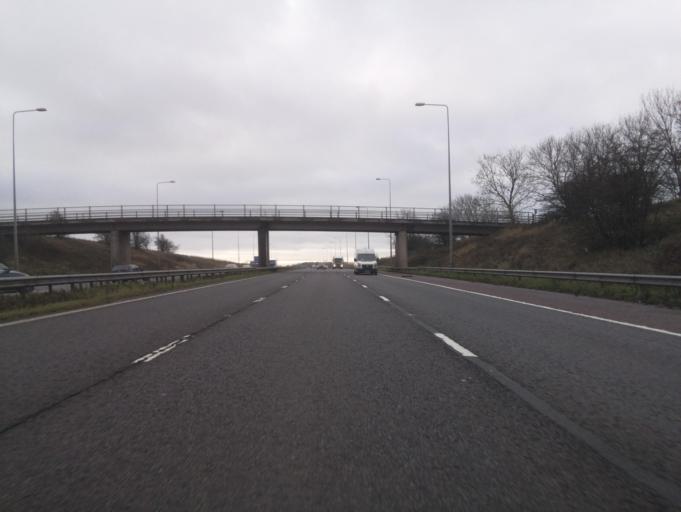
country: GB
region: England
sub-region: Lancashire
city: Euxton
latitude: 53.6437
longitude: -2.6926
